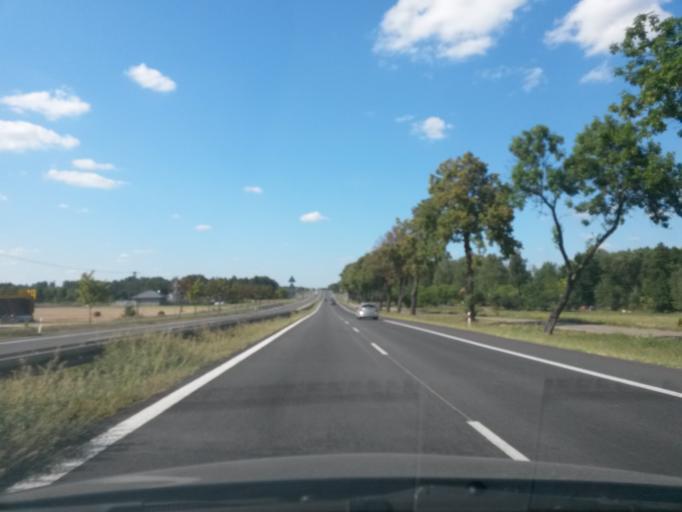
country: PL
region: Masovian Voivodeship
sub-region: Powiat plonski
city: Zaluski
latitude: 52.5617
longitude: 20.4918
